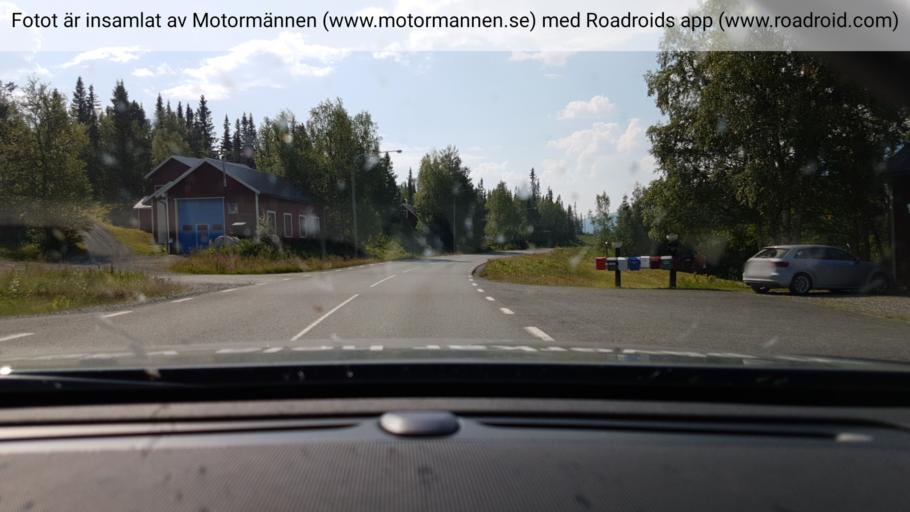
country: SE
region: Vaesterbotten
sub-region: Vilhelmina Kommun
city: Sjoberg
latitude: 65.6038
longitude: 15.5325
